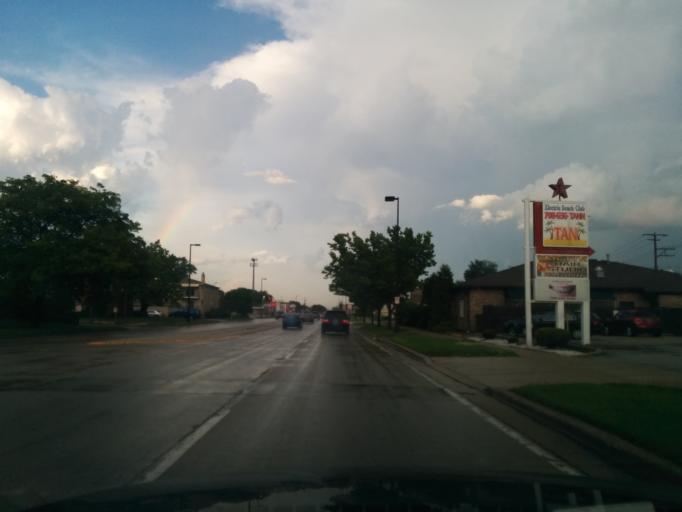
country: US
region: Illinois
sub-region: Cook County
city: Burbank
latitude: 41.7340
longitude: -87.7670
